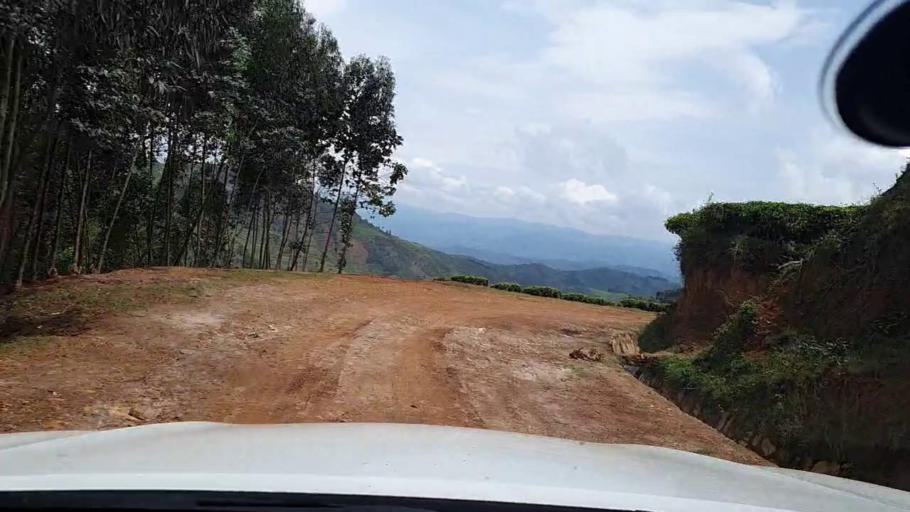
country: RW
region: Western Province
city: Kibuye
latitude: -2.1699
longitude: 29.3963
